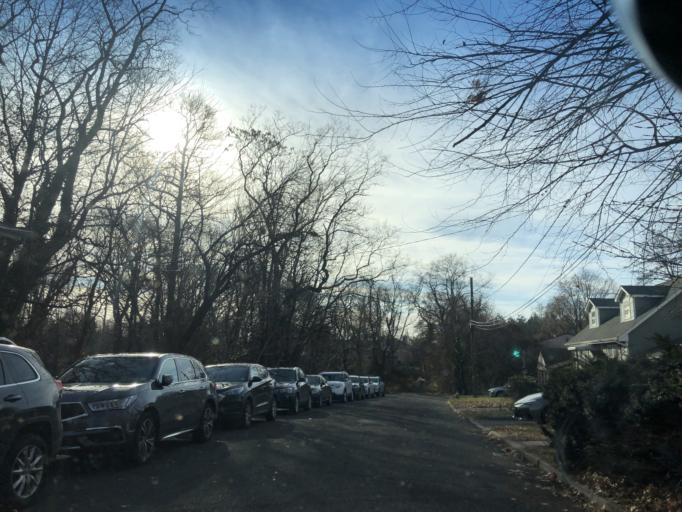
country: US
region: New Jersey
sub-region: Bergen County
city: Fair Lawn
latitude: 40.9268
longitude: -74.1269
